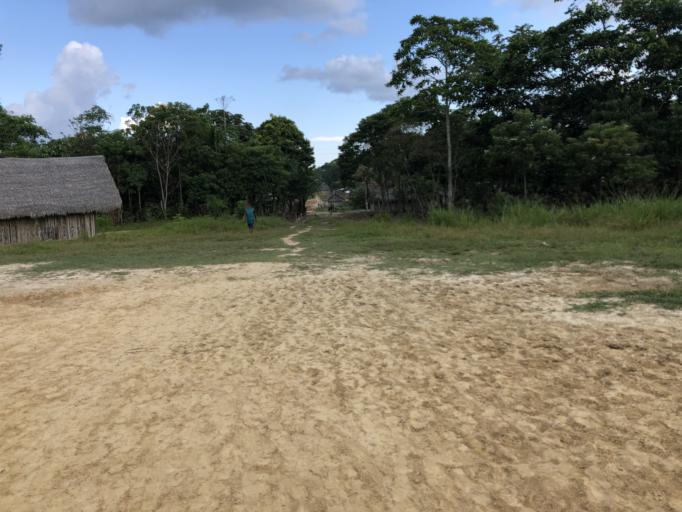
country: PE
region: Loreto
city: Puerto Galilea
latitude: -4.0557
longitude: -77.7613
